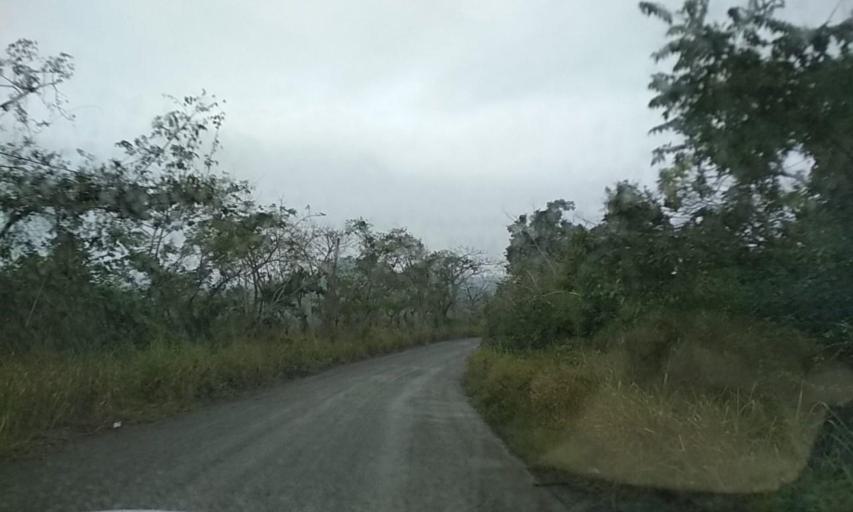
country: MX
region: Veracruz
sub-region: Coatzintla
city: Manuel Maria Contreras
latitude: 20.4541
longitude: -97.4743
